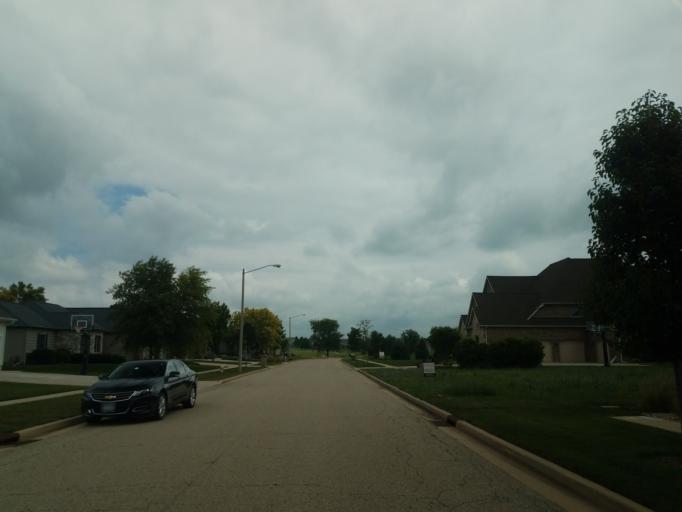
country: US
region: Illinois
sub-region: McLean County
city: Twin Grove
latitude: 40.4411
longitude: -89.0430
